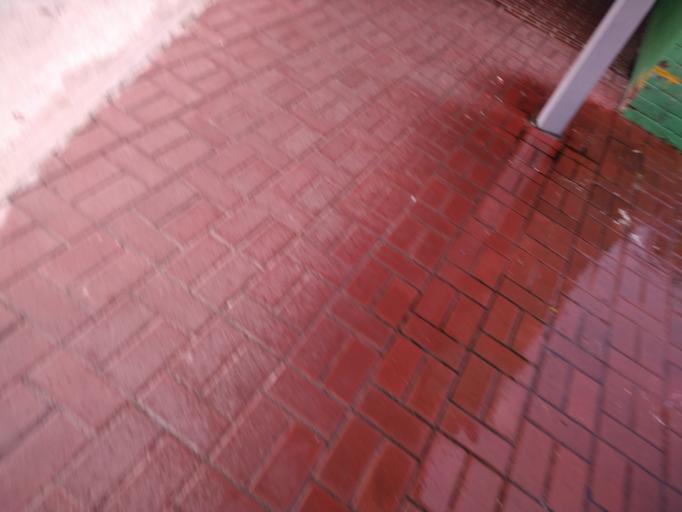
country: SG
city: Singapore
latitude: 1.2889
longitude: 103.8202
